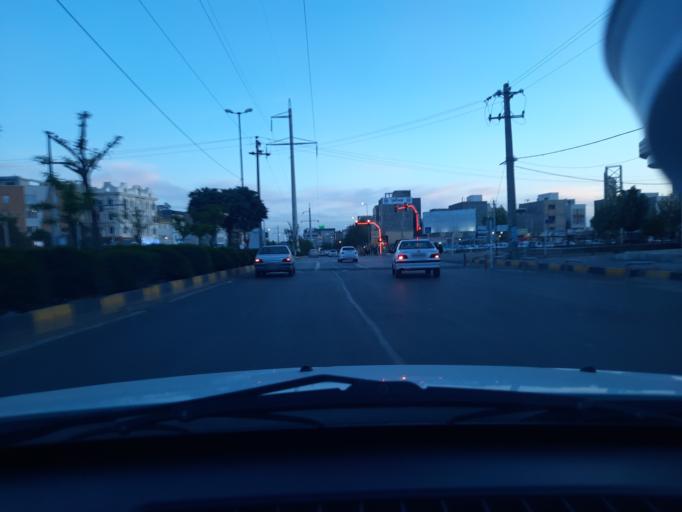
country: IR
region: Qazvin
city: Qazvin
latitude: 36.3025
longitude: 50.0104
